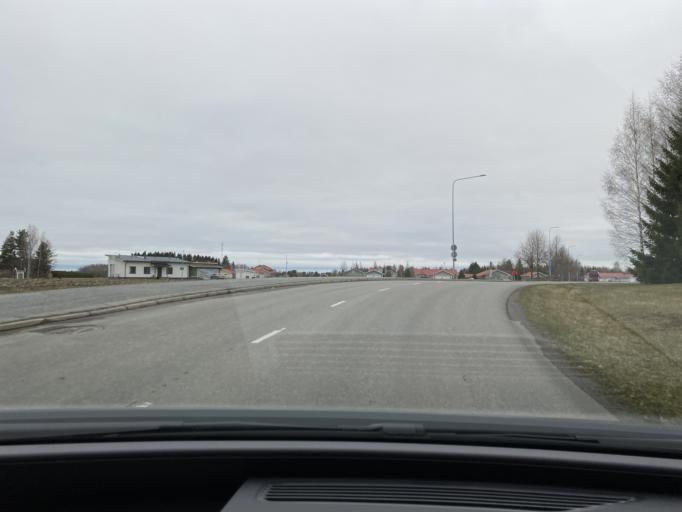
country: FI
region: Satakunta
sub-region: Pori
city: Huittinen
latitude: 61.1829
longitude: 22.6830
